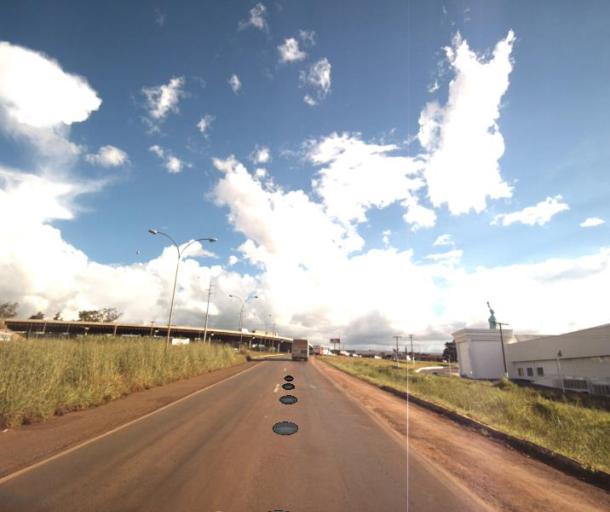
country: BR
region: Goias
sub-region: Anapolis
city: Anapolis
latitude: -16.3520
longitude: -48.9286
